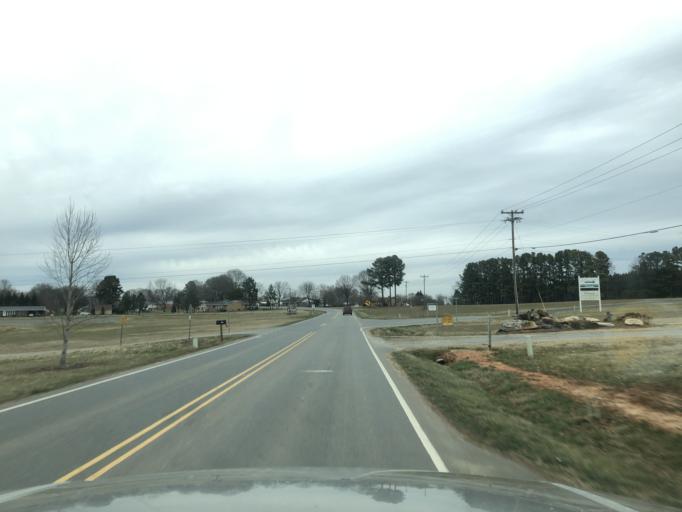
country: US
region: North Carolina
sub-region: Cleveland County
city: Shelby
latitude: 35.3242
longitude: -81.4956
